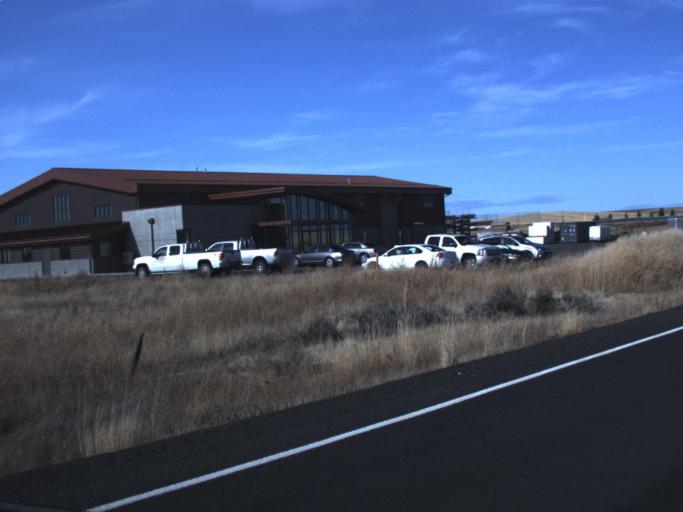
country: US
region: Washington
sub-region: Lincoln County
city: Davenport
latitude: 47.6603
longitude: -118.1410
